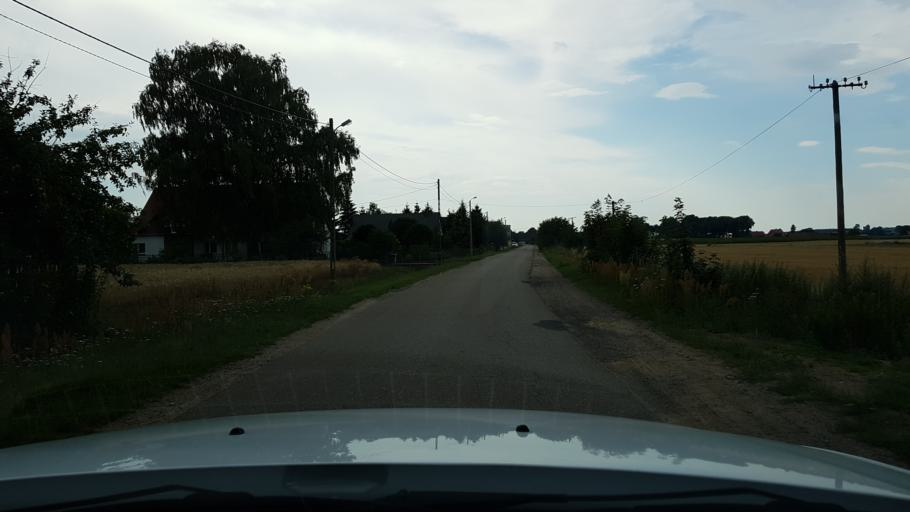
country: PL
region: West Pomeranian Voivodeship
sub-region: Powiat walecki
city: Walcz
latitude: 53.3730
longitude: 16.3275
